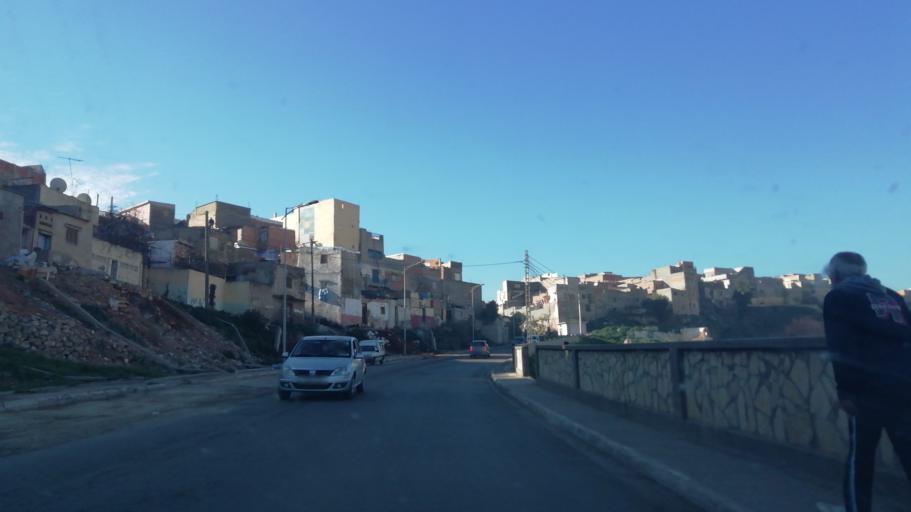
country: DZ
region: Oran
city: Oran
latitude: 35.6874
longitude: -0.6687
